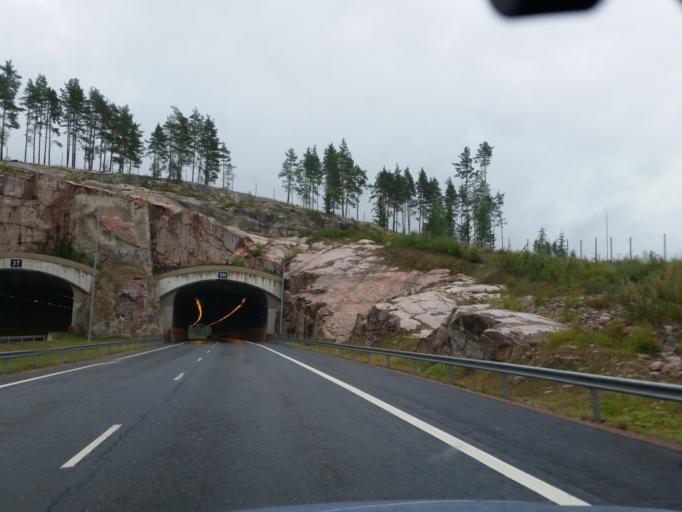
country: FI
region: Varsinais-Suomi
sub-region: Salo
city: Muurla
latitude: 60.3760
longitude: 23.3340
